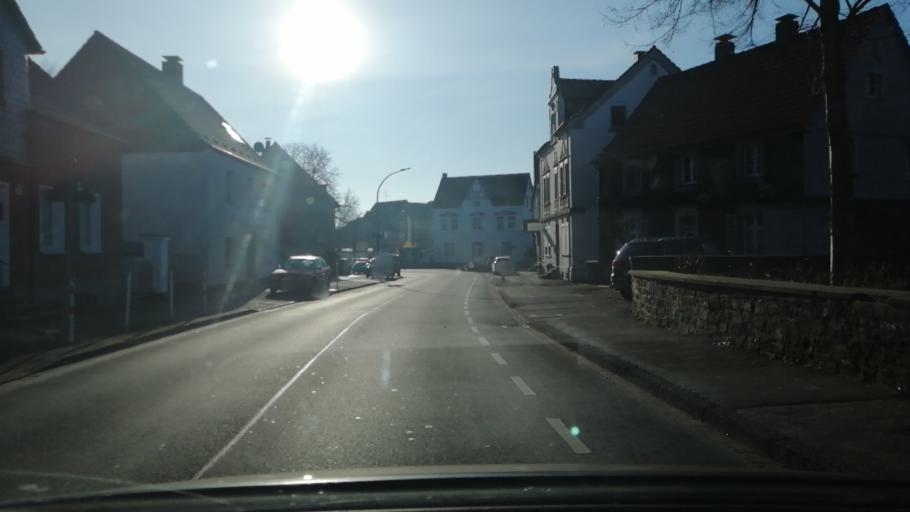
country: DE
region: North Rhine-Westphalia
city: Schwerte
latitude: 51.4964
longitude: 7.5612
